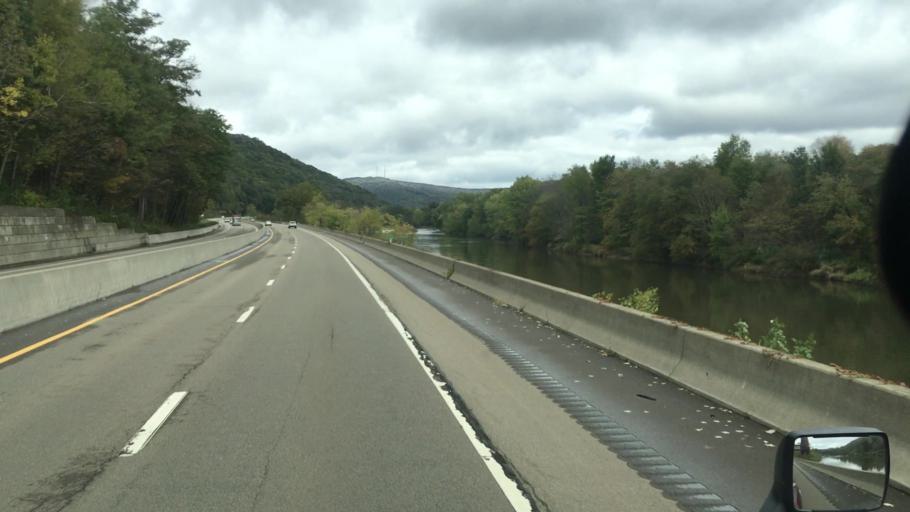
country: US
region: New York
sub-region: Cattaraugus County
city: Salamanca
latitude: 42.1180
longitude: -78.6635
